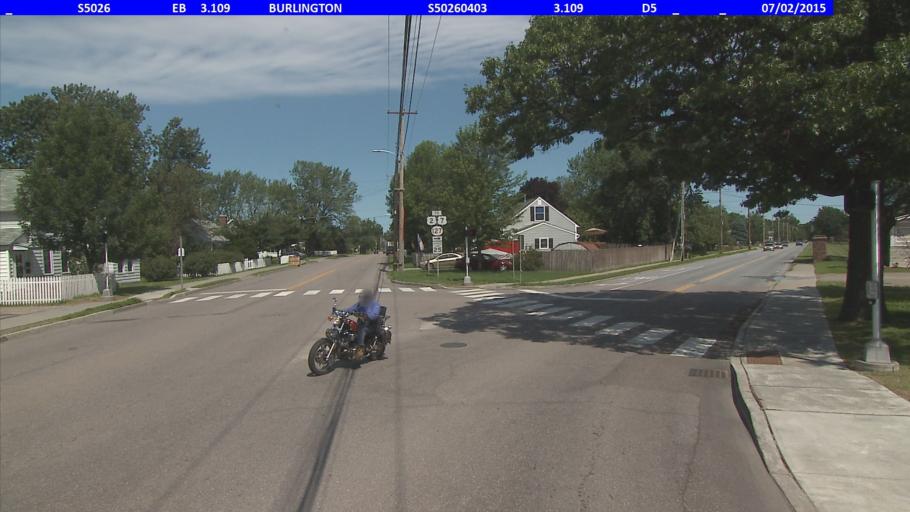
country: US
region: Vermont
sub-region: Chittenden County
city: Burlington
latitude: 44.5158
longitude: -73.2568
